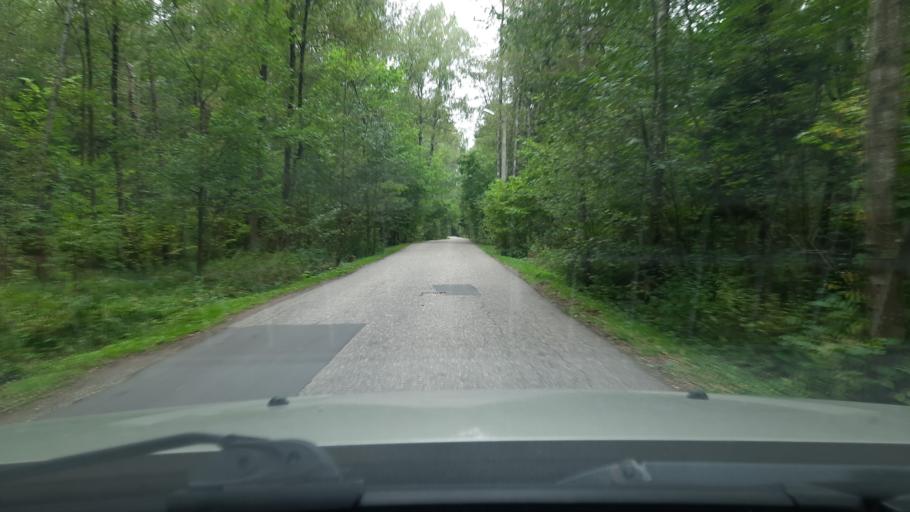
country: RU
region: Moskovskaya
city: Odintsovo
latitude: 55.7081
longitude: 37.3052
